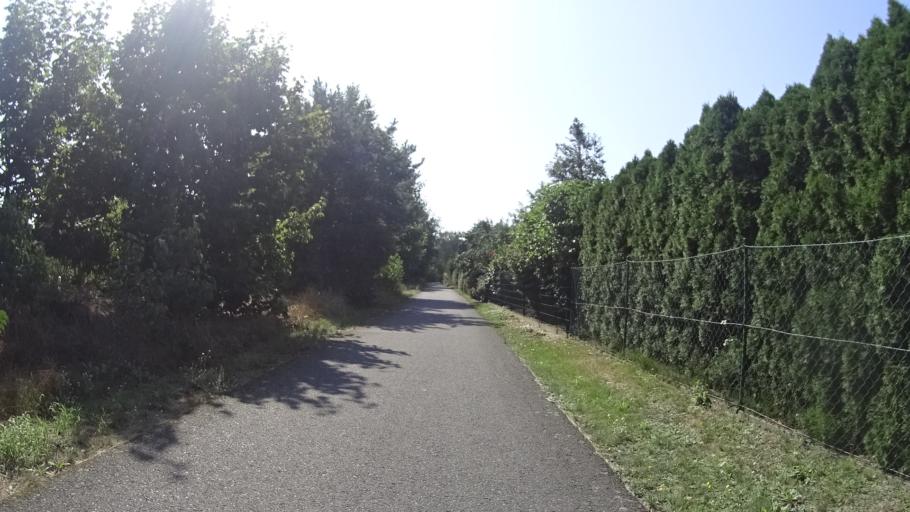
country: DE
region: Brandenburg
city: Cottbus
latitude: 51.7911
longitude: 14.3039
